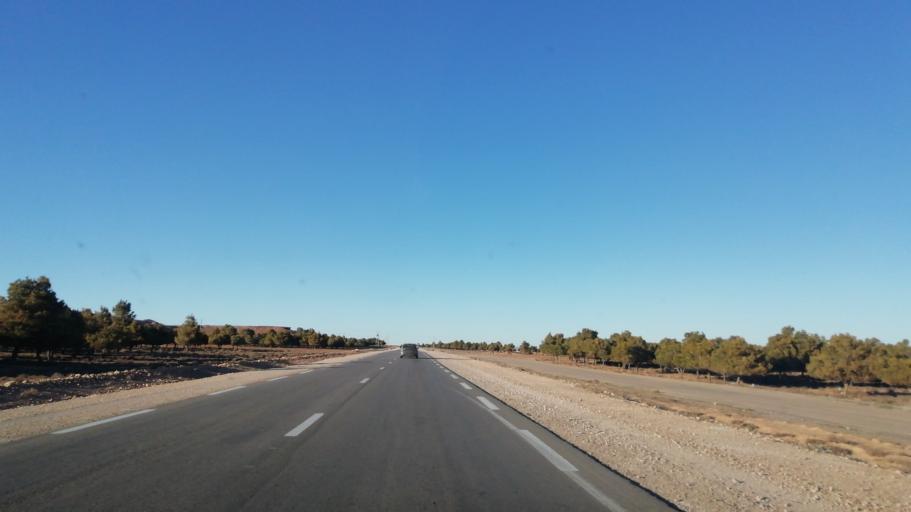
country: DZ
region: Tlemcen
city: Sebdou
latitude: 34.4964
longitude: -1.2759
